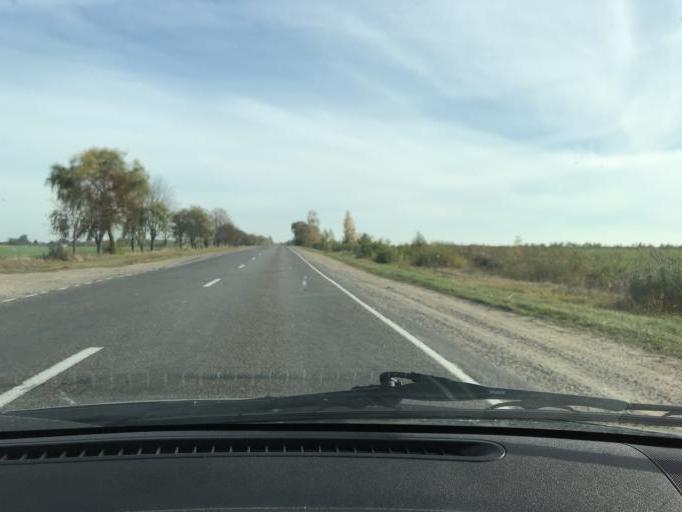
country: BY
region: Brest
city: Asnyezhytsy
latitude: 52.2064
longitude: 26.0542
